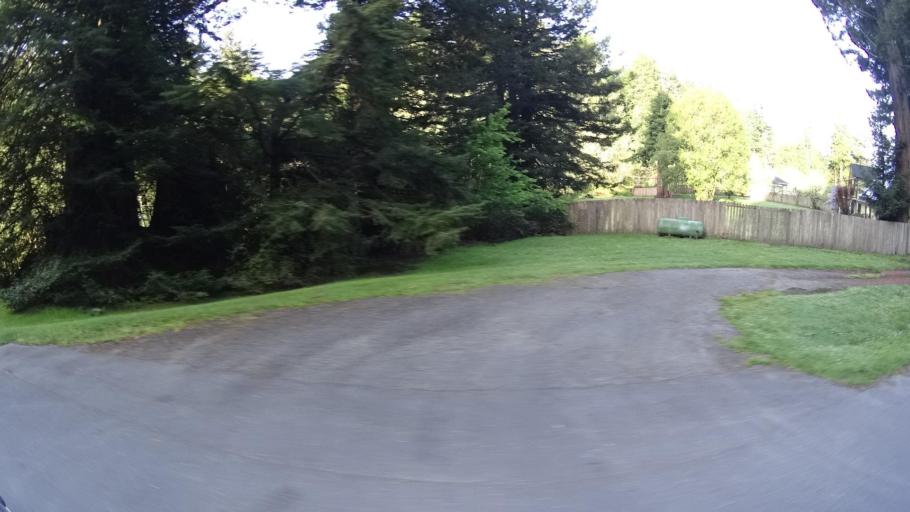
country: US
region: California
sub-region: Humboldt County
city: Bayside
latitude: 40.7583
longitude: -124.0498
